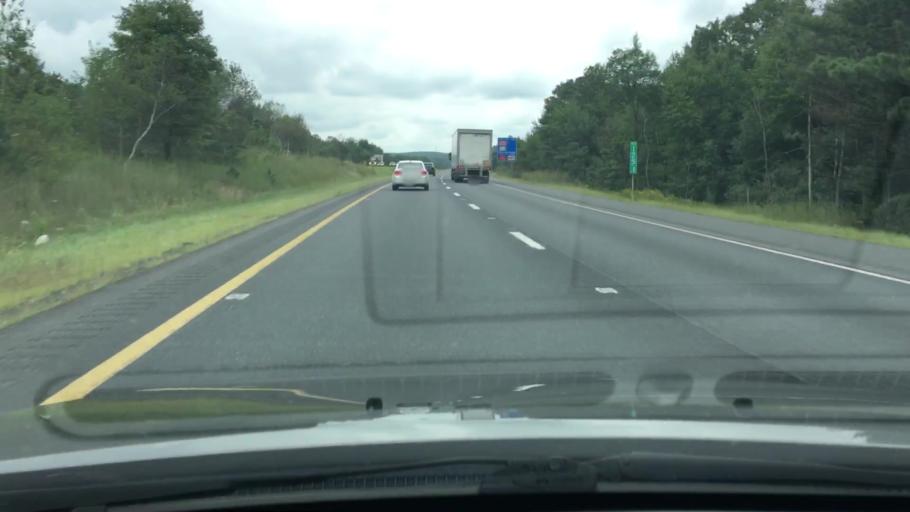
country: US
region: Pennsylvania
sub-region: Schuylkill County
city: Frackville
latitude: 40.7746
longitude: -76.2034
